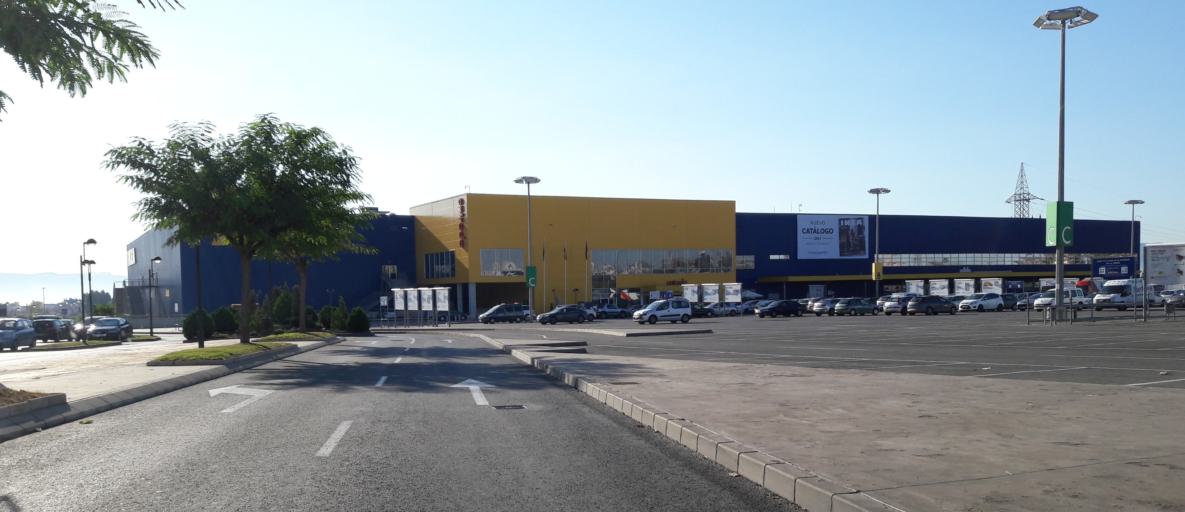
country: ES
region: Murcia
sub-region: Murcia
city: Murcia
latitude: 38.0290
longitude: -1.1463
